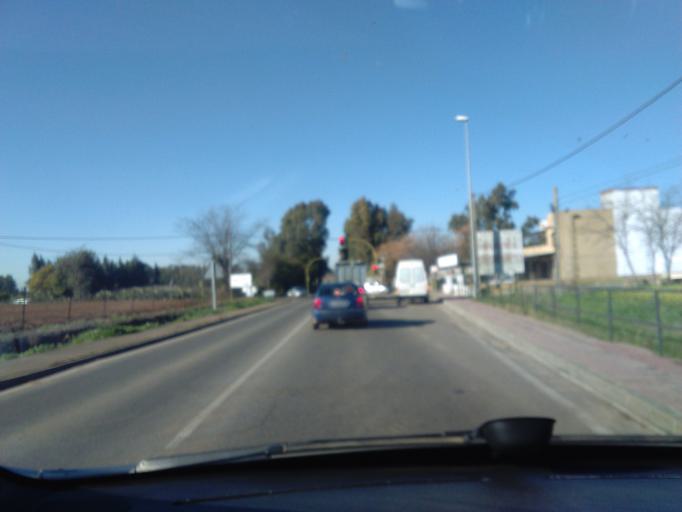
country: ES
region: Andalusia
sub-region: Provincia de Sevilla
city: Sevilla
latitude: 37.4286
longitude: -5.9309
